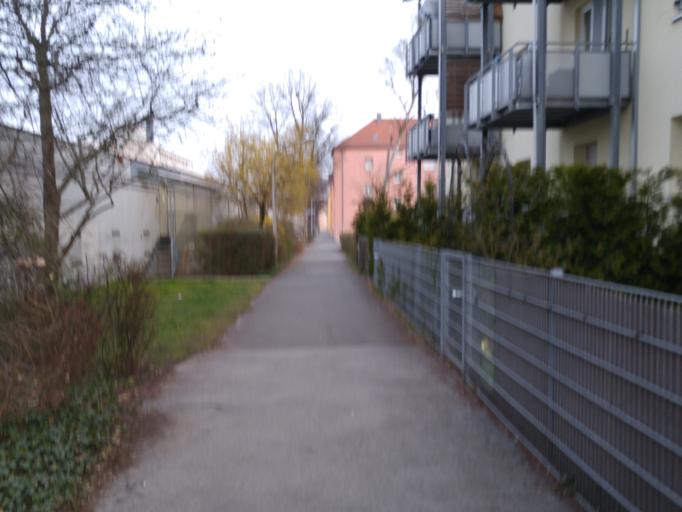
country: DE
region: Bavaria
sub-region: Regierungsbezirk Mittelfranken
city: Nuernberg
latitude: 49.4690
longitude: 11.1127
